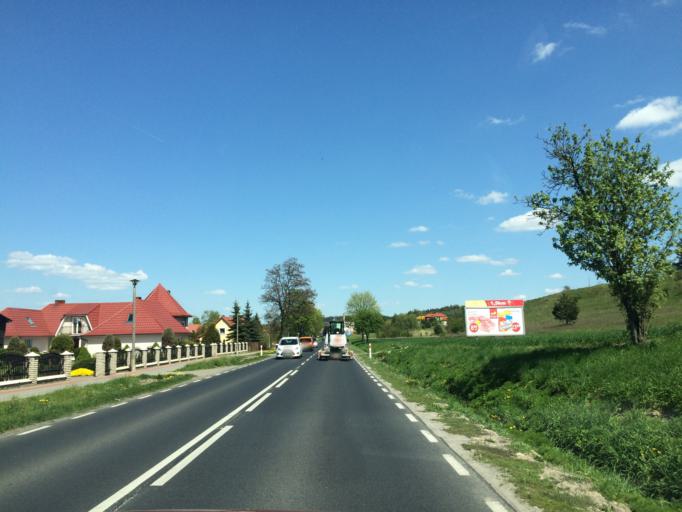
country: PL
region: Warmian-Masurian Voivodeship
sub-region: Powiat nowomiejski
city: Kurzetnik
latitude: 53.4024
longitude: 19.5867
